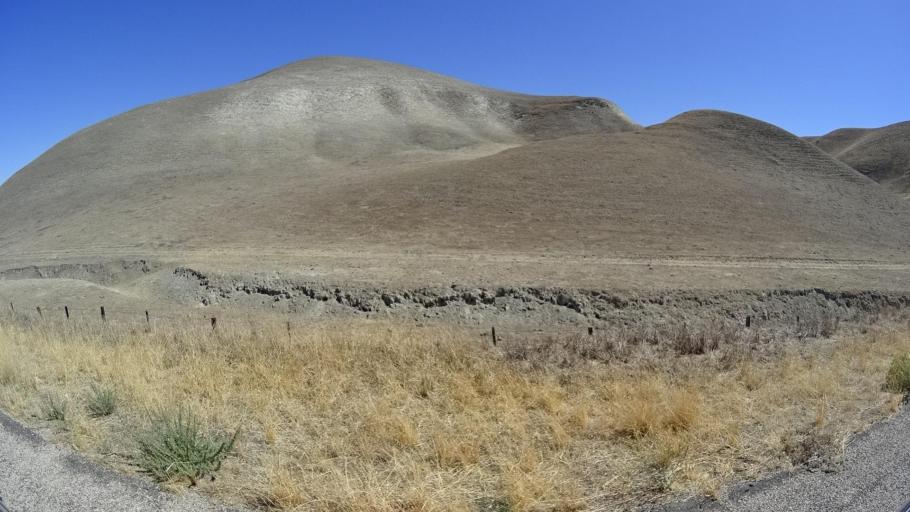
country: US
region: California
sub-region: Monterey County
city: King City
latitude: 36.2528
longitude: -120.9992
